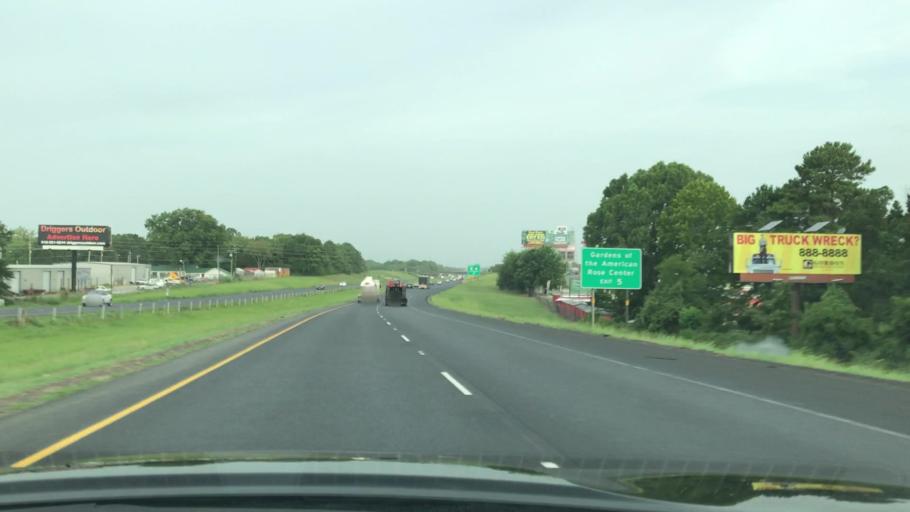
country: US
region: Louisiana
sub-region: Caddo Parish
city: Greenwood
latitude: 32.4437
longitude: -93.9411
